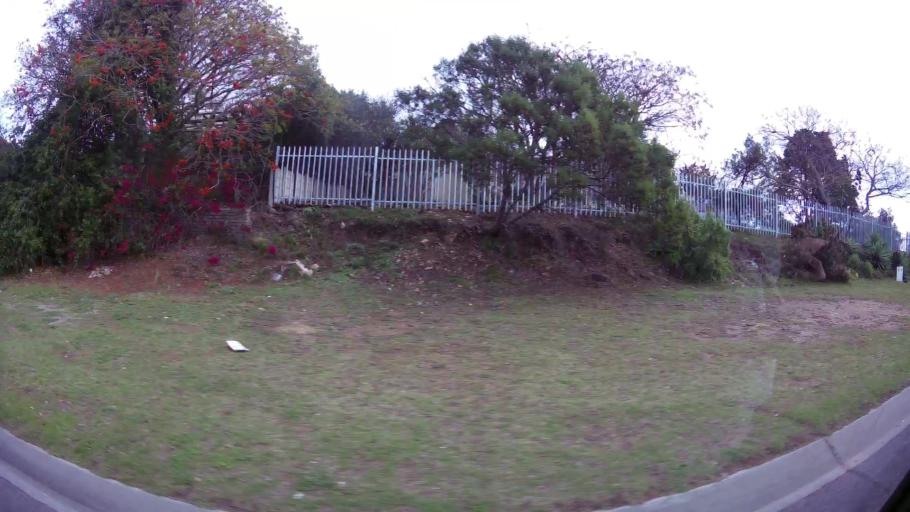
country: ZA
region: Eastern Cape
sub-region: Nelson Mandela Bay Metropolitan Municipality
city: Port Elizabeth
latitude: -33.9336
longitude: 25.5204
